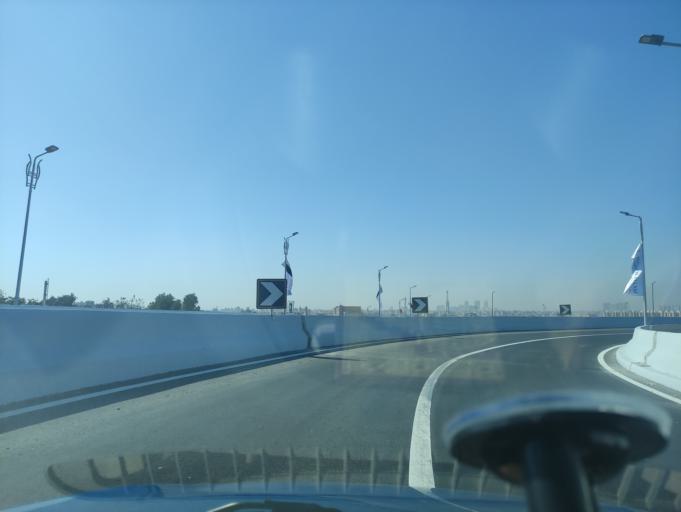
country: EG
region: Muhafazat al Qahirah
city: Cairo
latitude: 30.0080
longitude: 31.2714
